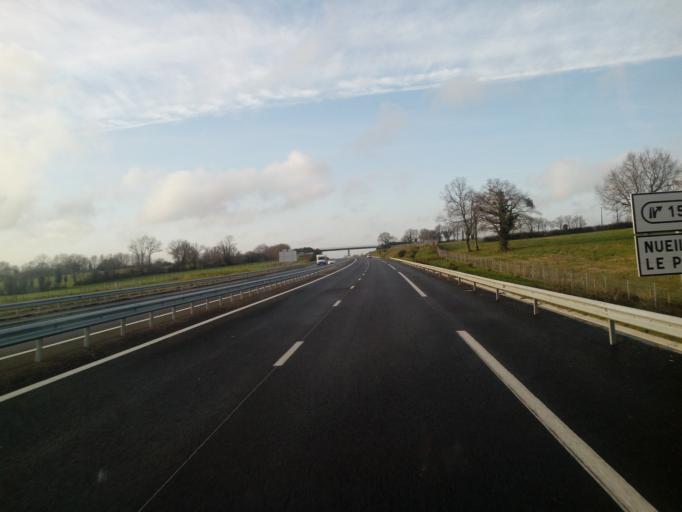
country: FR
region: Poitou-Charentes
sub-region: Departement des Deux-Sevres
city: Le Pin
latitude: 46.8925
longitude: -0.6143
